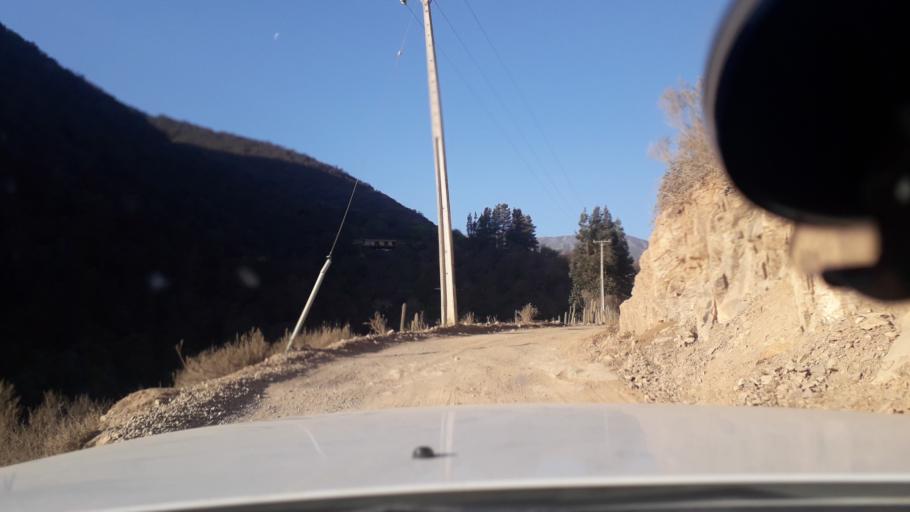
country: CL
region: Valparaiso
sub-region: Provincia de Marga Marga
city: Limache
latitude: -33.0522
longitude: -71.0733
